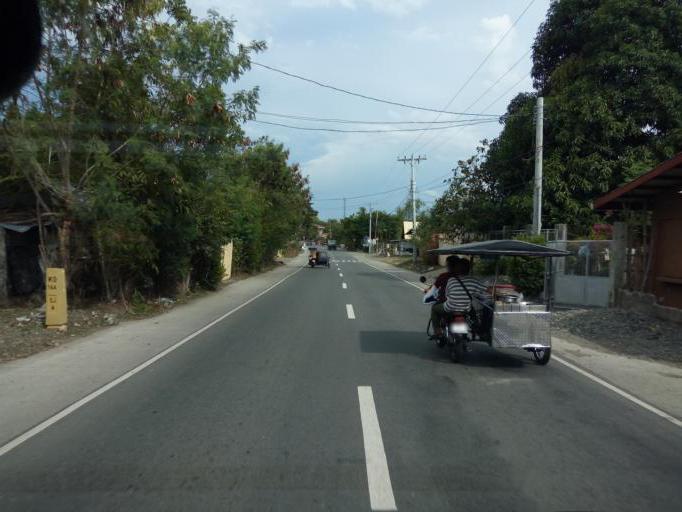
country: PH
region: Central Luzon
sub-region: Province of Nueva Ecija
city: Sibul
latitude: 15.8176
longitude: 120.9579
